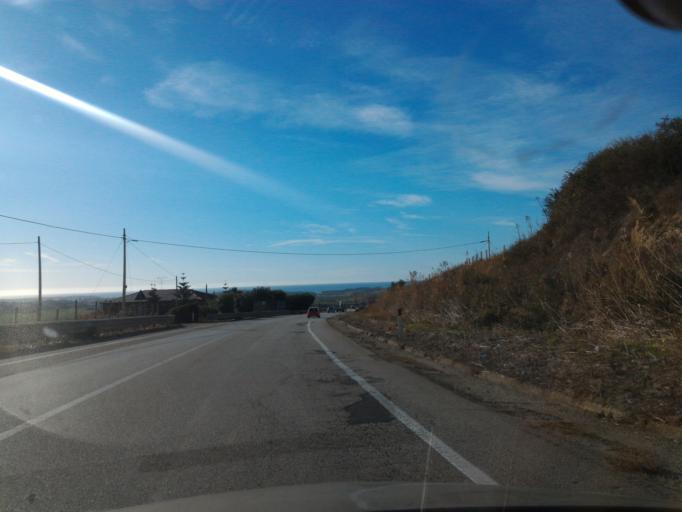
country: IT
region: Calabria
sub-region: Provincia di Crotone
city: Isola di Capo Rizzuto
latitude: 38.9483
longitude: 17.0826
